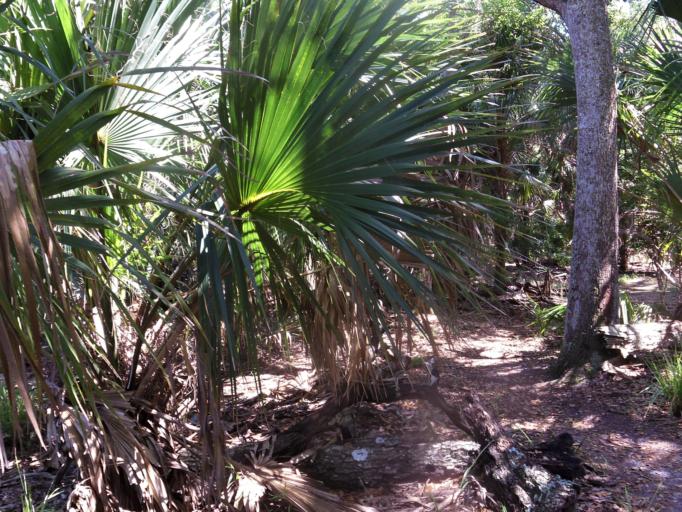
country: US
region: Florida
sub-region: Flagler County
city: Flagler Beach
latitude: 29.4340
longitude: -81.1368
